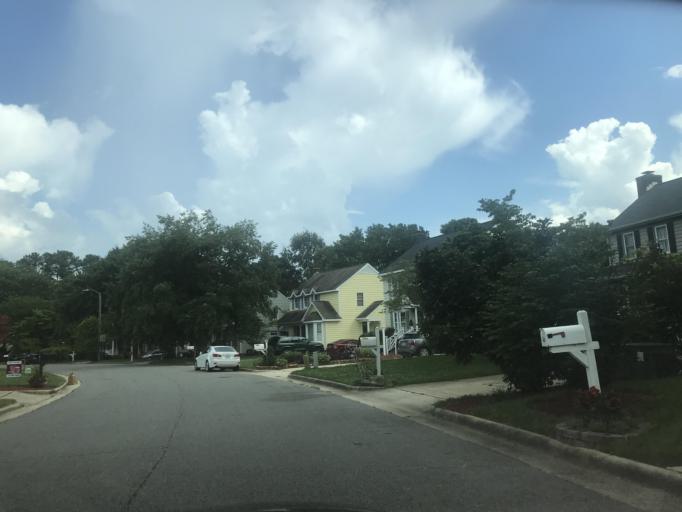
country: US
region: North Carolina
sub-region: Wake County
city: Raleigh
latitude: 35.8330
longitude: -78.5671
